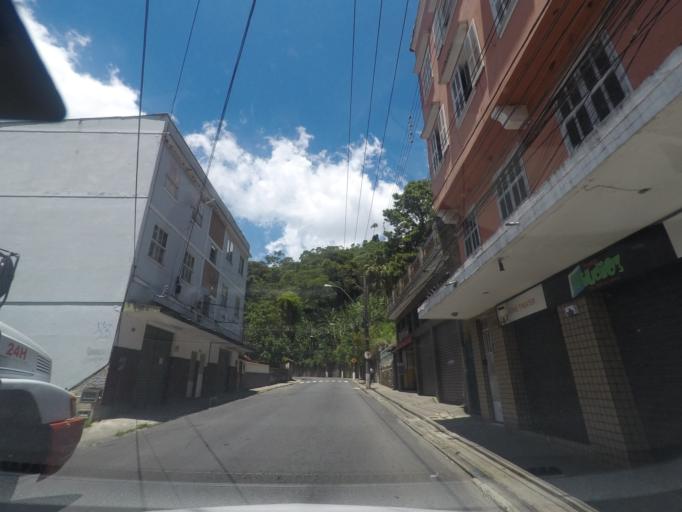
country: BR
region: Rio de Janeiro
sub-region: Petropolis
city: Petropolis
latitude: -22.5128
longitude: -43.1735
